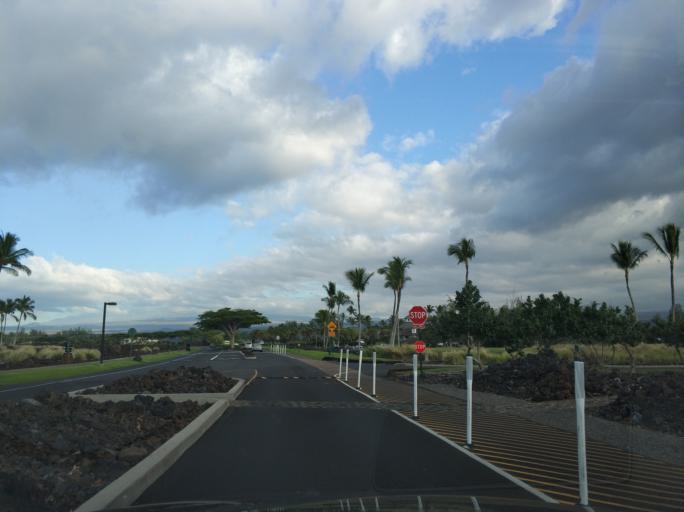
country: US
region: Hawaii
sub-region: Hawaii County
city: Waikoloa Village
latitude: 19.9225
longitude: -155.8765
